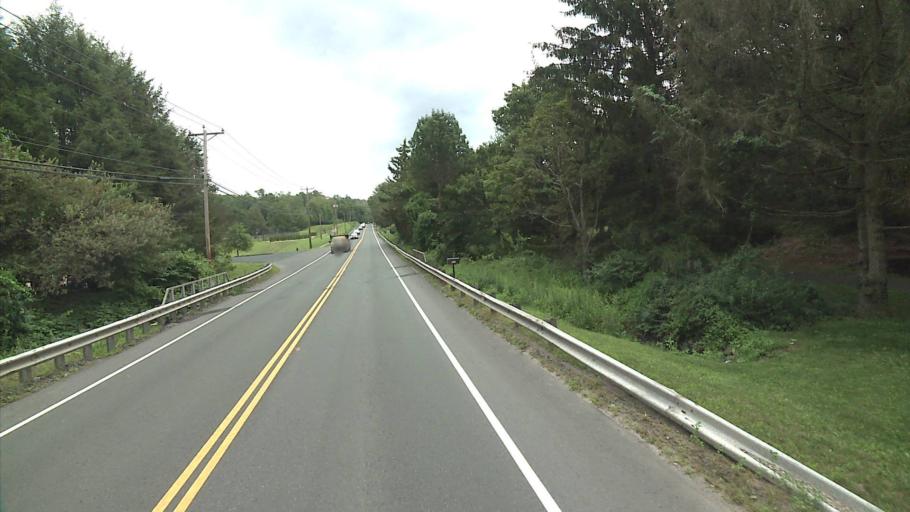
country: US
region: Connecticut
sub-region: New Haven County
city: Southbury
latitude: 41.4761
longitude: -73.2028
